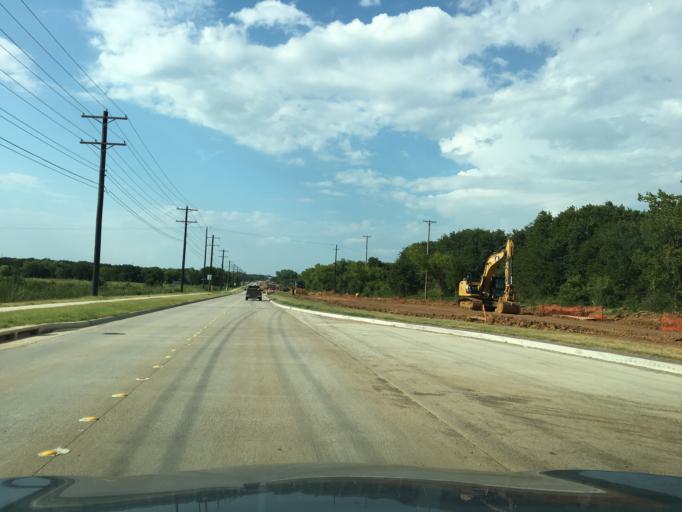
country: US
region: Texas
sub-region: Denton County
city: Denton
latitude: 33.2184
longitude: -97.0836
